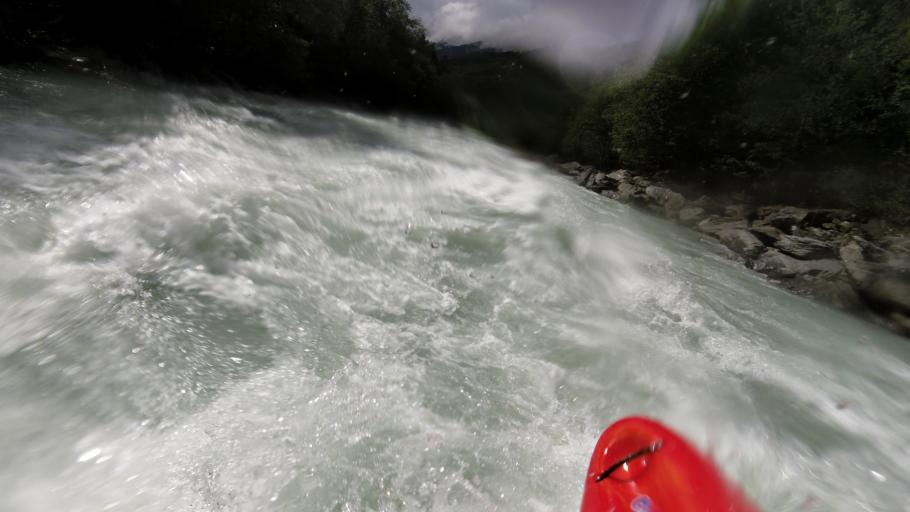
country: AT
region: Tyrol
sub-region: Politischer Bezirk Landeck
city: Zams
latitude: 47.1195
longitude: 10.6033
